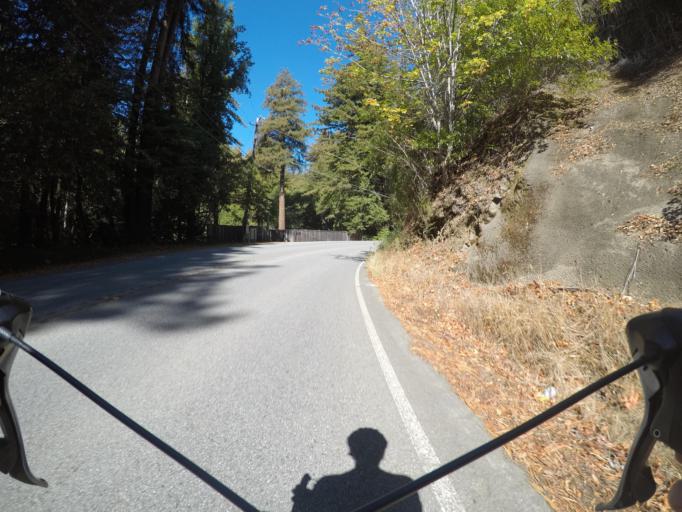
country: US
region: California
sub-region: San Mateo County
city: Portola Valley
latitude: 37.3366
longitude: -122.2691
